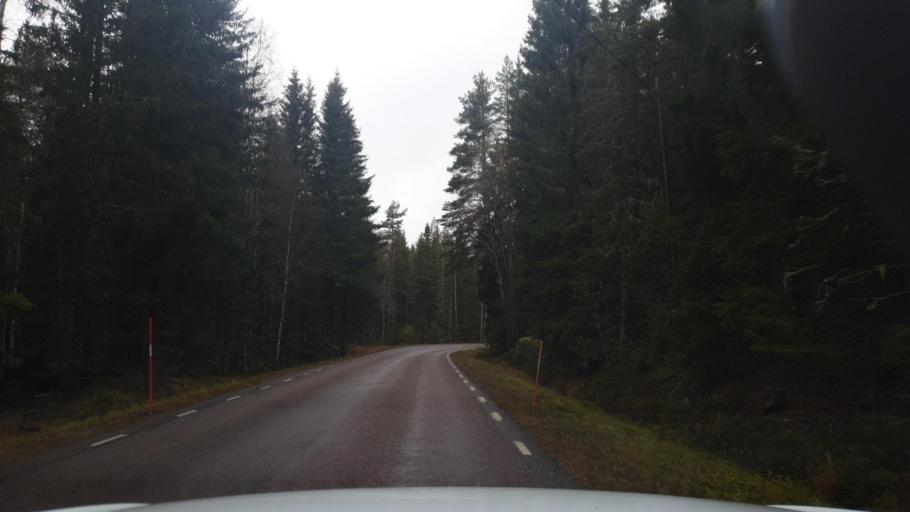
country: NO
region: Hedmark
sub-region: Eidskog
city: Skotterud
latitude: 59.8099
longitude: 12.0576
